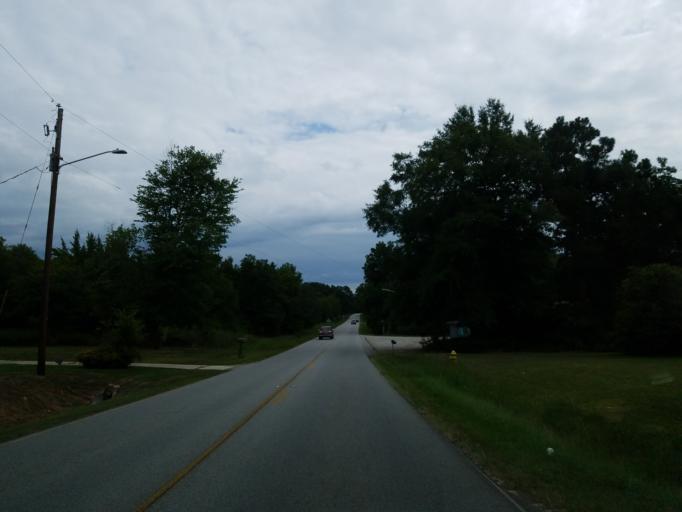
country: US
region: Georgia
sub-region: Henry County
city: Hampton
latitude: 33.3402
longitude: -84.2908
